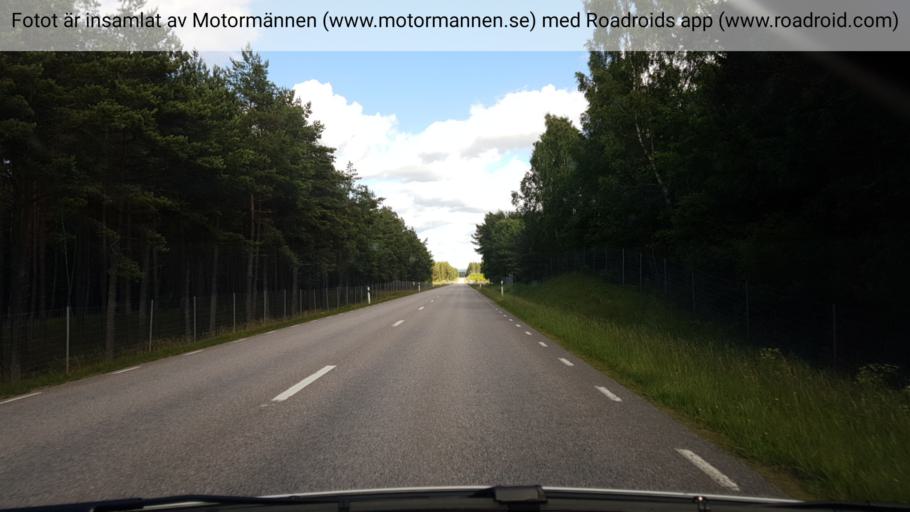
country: SE
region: Vaestra Goetaland
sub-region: Vara Kommun
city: Kvanum
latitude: 58.2125
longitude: 13.2471
